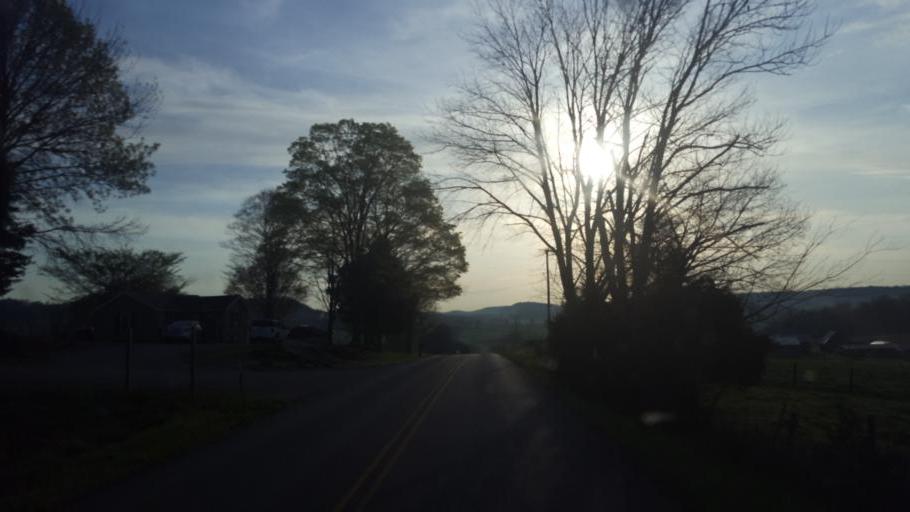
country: US
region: Kentucky
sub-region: Hart County
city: Horse Cave
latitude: 37.2198
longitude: -85.9594
